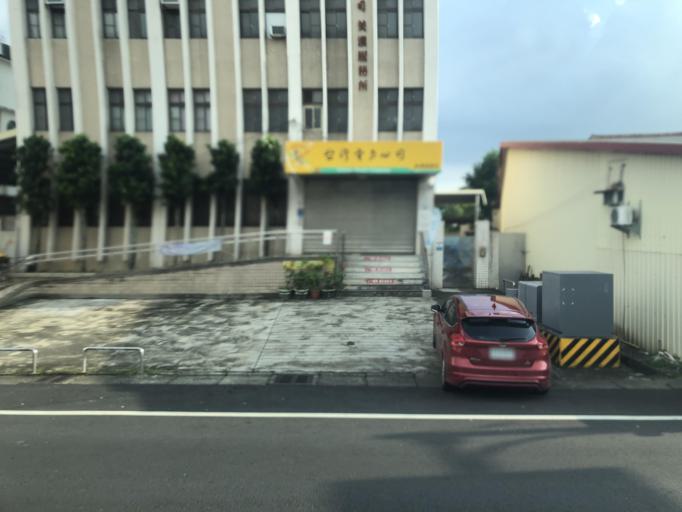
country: TW
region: Taiwan
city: Yujing
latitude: 22.9022
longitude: 120.5406
